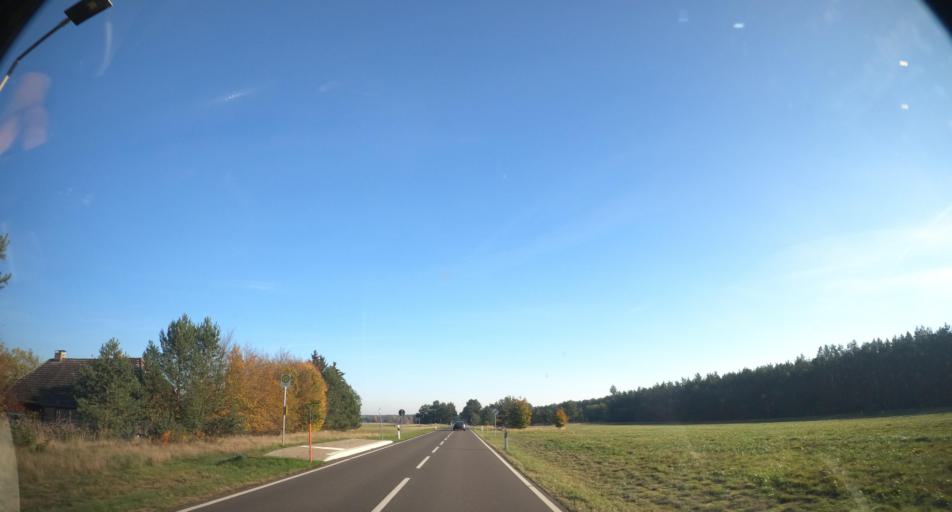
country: DE
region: Mecklenburg-Vorpommern
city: Ahlbeck
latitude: 53.6225
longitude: 14.2342
